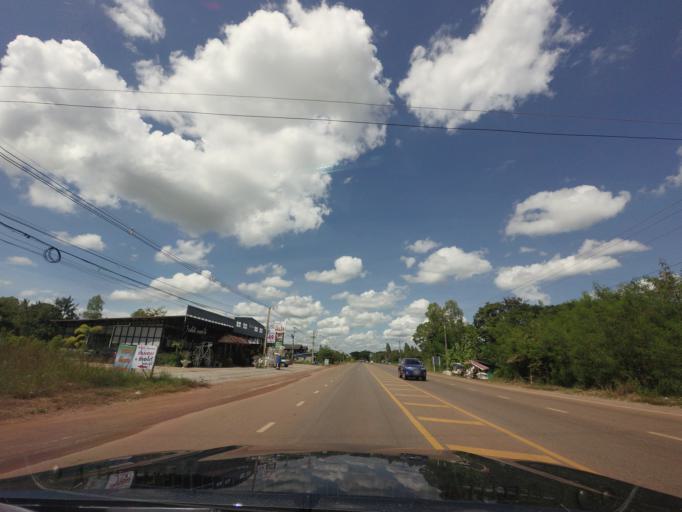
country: TH
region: Changwat Udon Thani
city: Ban Dung
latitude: 17.7277
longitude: 103.2515
